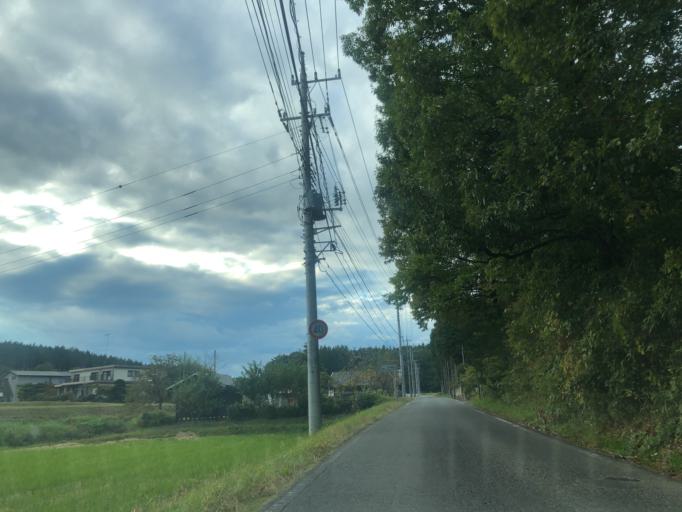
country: JP
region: Tochigi
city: Kuroiso
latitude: 36.9410
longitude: 140.1163
